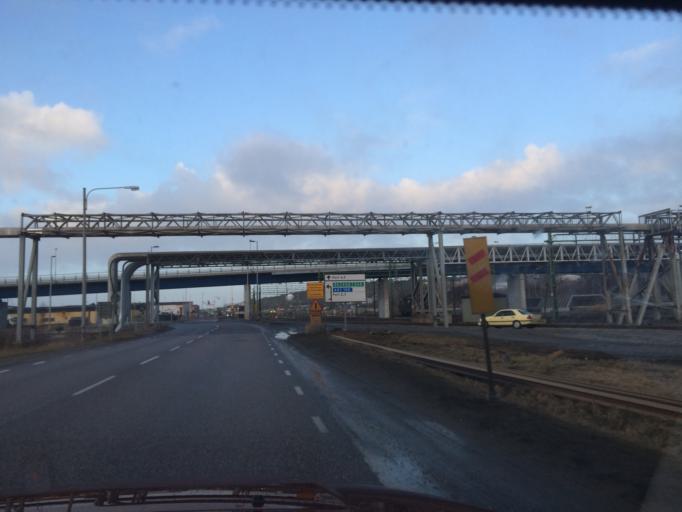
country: SE
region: Vaestra Goetaland
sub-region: Goteborg
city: Majorna
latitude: 57.6987
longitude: 11.8625
